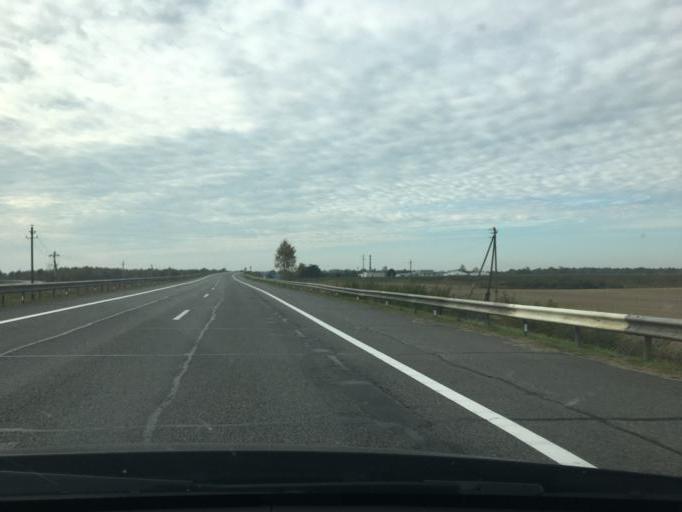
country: BY
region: Minsk
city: Stan'kava
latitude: 53.6779
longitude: 27.1979
